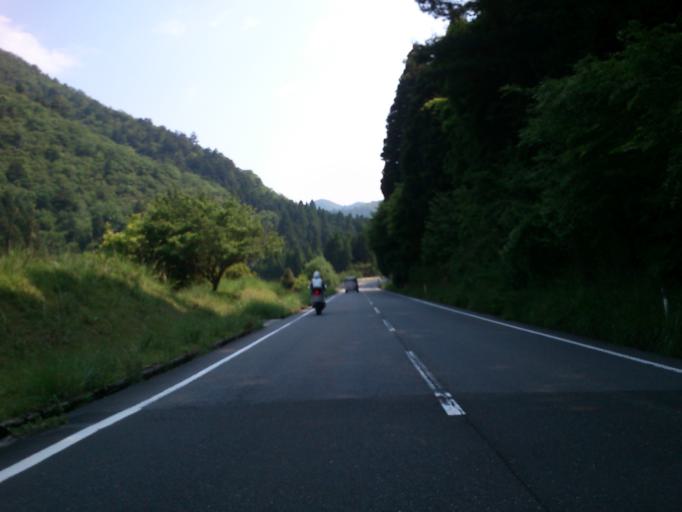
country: JP
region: Kyoto
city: Kameoka
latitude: 35.2507
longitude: 135.5615
